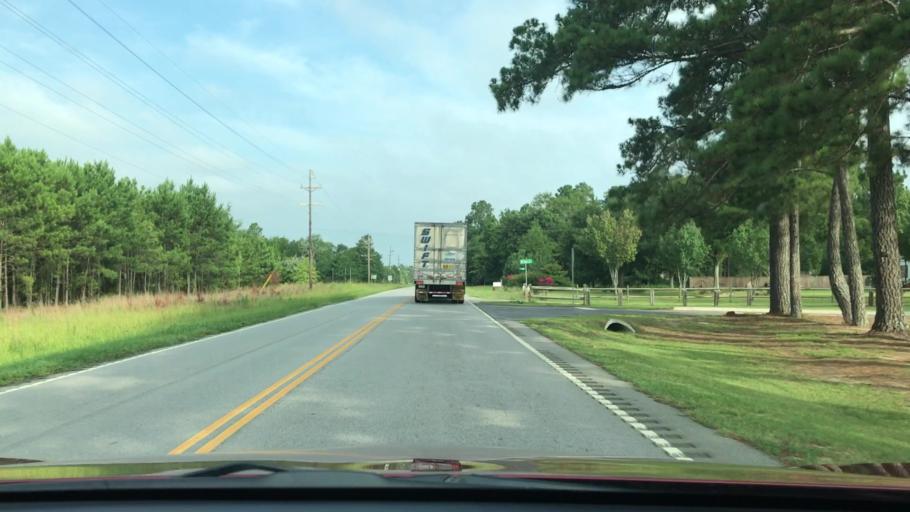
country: US
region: South Carolina
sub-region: Barnwell County
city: Williston
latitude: 33.6420
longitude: -81.3381
